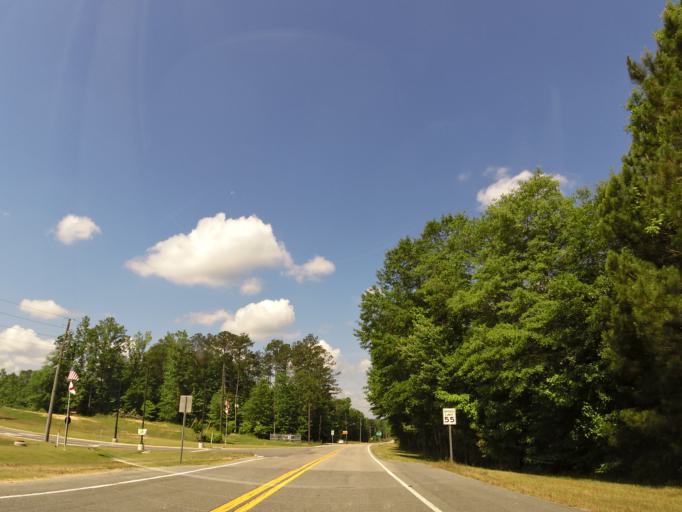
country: US
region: Alabama
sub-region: Marion County
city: Winfield
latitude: 34.0113
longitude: -87.8379
